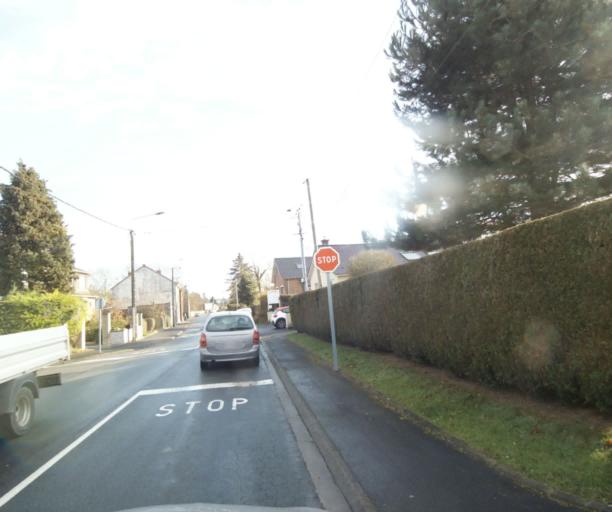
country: FR
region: Nord-Pas-de-Calais
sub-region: Departement du Nord
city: Maing
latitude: 50.3048
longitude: 3.4718
